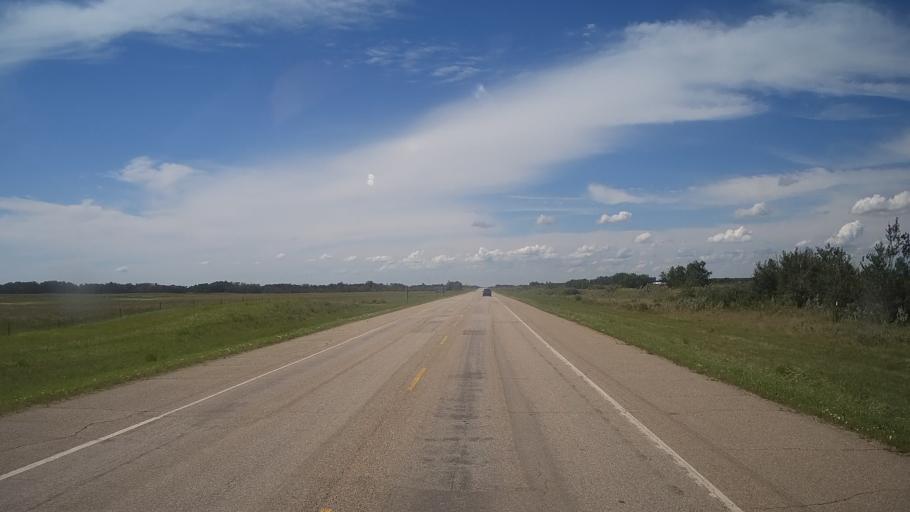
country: CA
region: Saskatchewan
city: Yorkton
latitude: 51.0504
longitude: -102.1828
